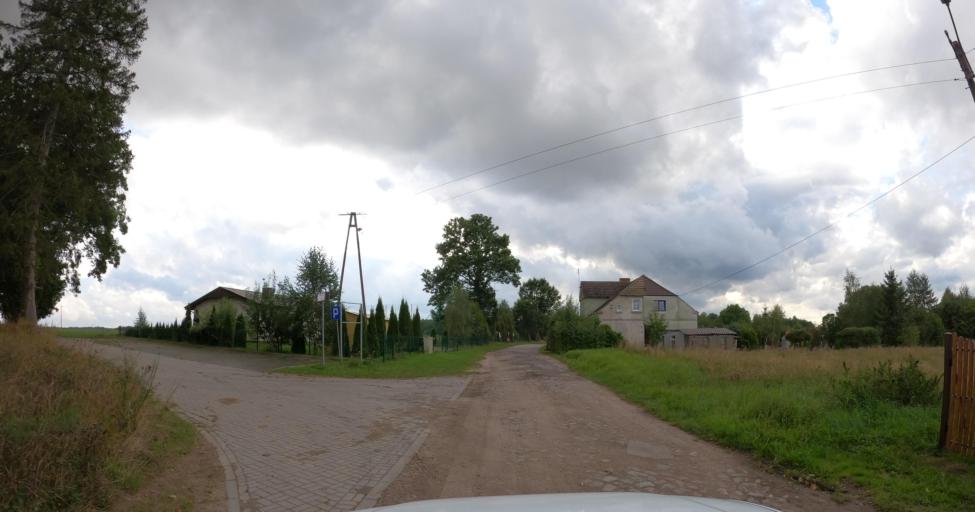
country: PL
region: West Pomeranian Voivodeship
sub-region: Powiat kolobrzeski
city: Goscino
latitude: 54.0756
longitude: 15.6047
